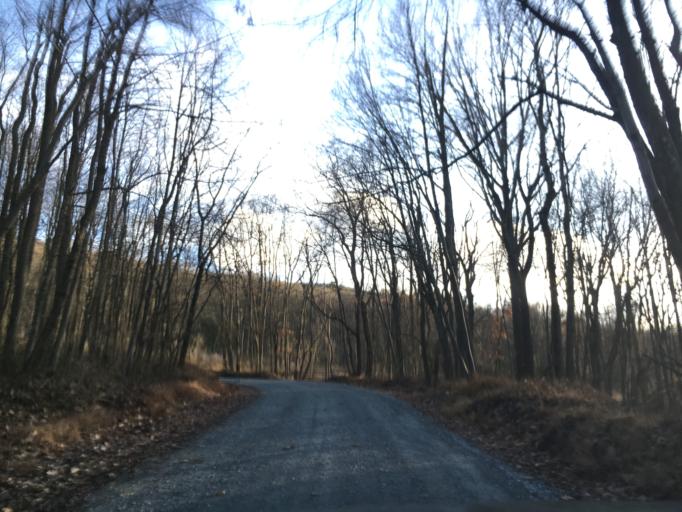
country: US
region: Pennsylvania
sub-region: Carbon County
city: Lehighton
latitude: 40.7693
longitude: -75.7105
